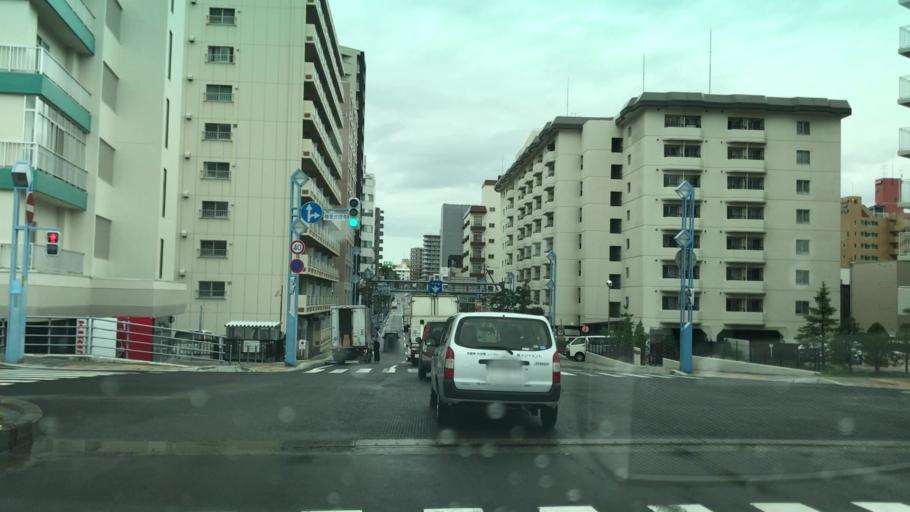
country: JP
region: Hokkaido
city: Sapporo
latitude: 43.0390
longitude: 141.3586
